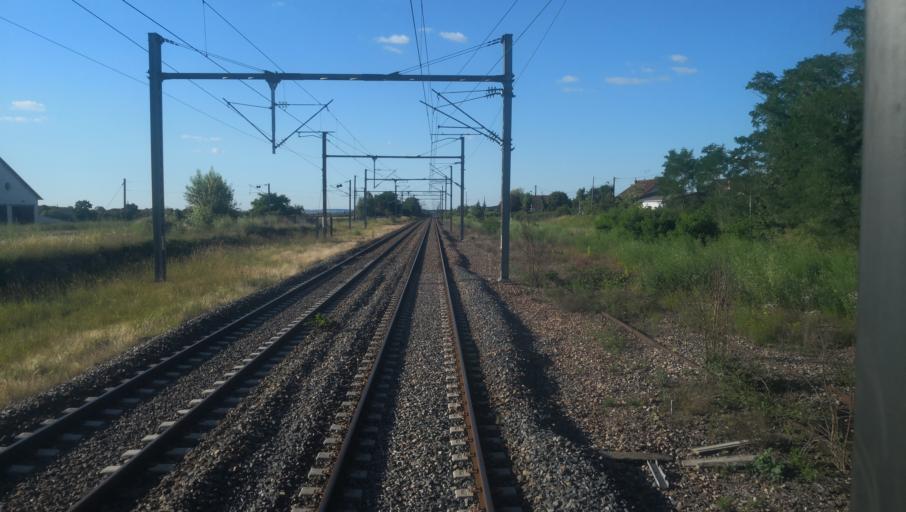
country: FR
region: Bourgogne
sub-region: Departement de la Nievre
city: Saint-Pierre-le-Moutier
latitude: 46.7949
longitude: 3.1116
